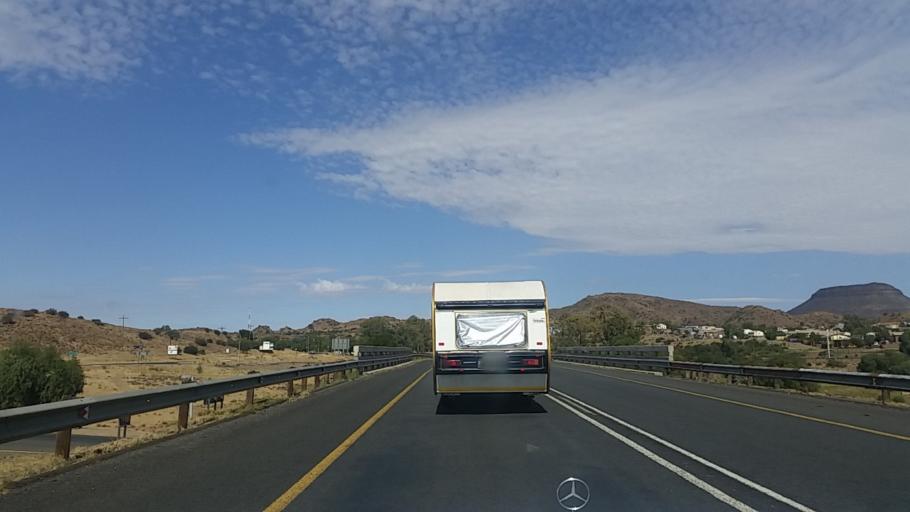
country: ZA
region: Northern Cape
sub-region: Pixley ka Seme District Municipality
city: Colesberg
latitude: -30.7096
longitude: 25.1056
